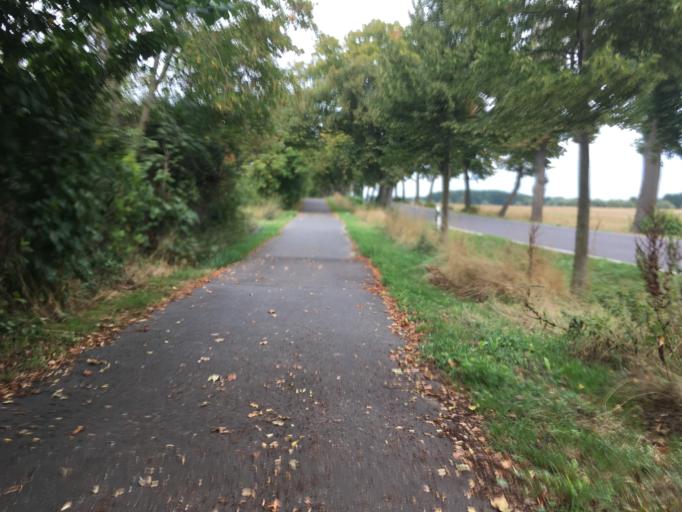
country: DE
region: Brandenburg
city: Prenzlau
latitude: 53.2355
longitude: 13.8433
